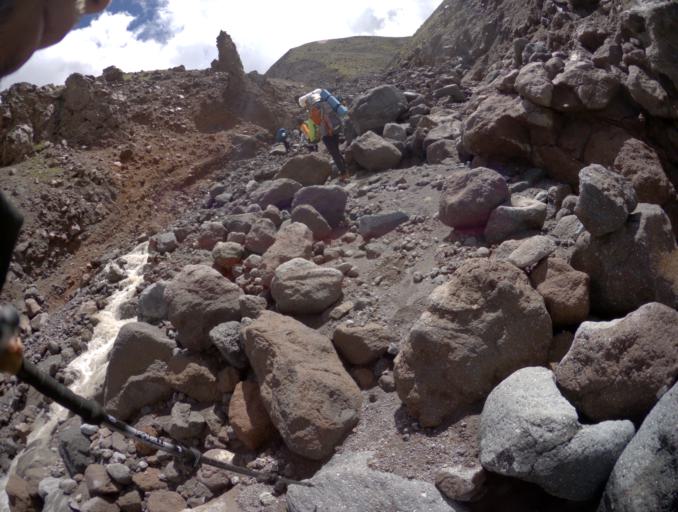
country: RU
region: Kabardino-Balkariya
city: Terskol
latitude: 43.3842
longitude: 42.3677
